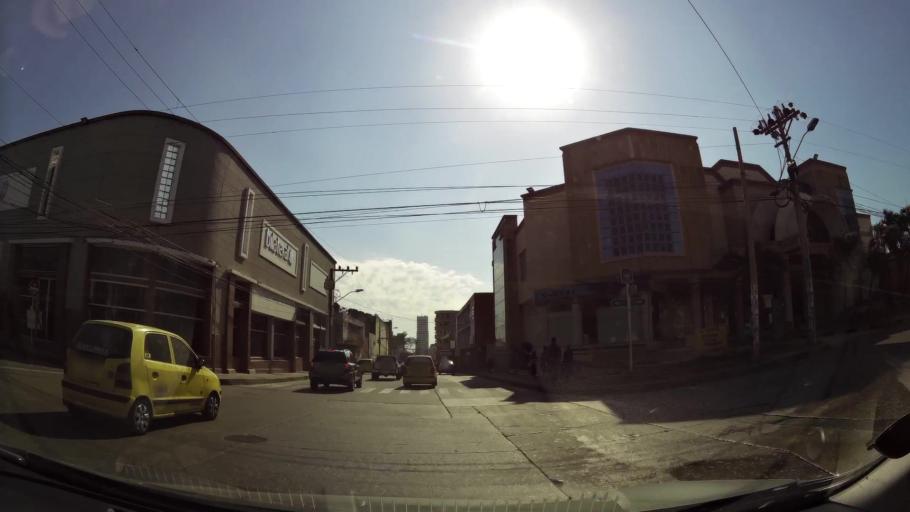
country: CO
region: Atlantico
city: Barranquilla
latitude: 10.9848
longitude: -74.7869
